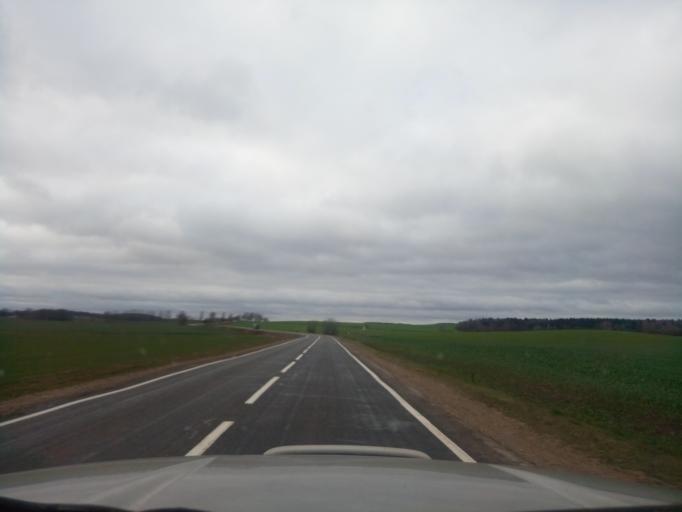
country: BY
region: Minsk
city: Kapyl'
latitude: 53.1896
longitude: 27.1858
